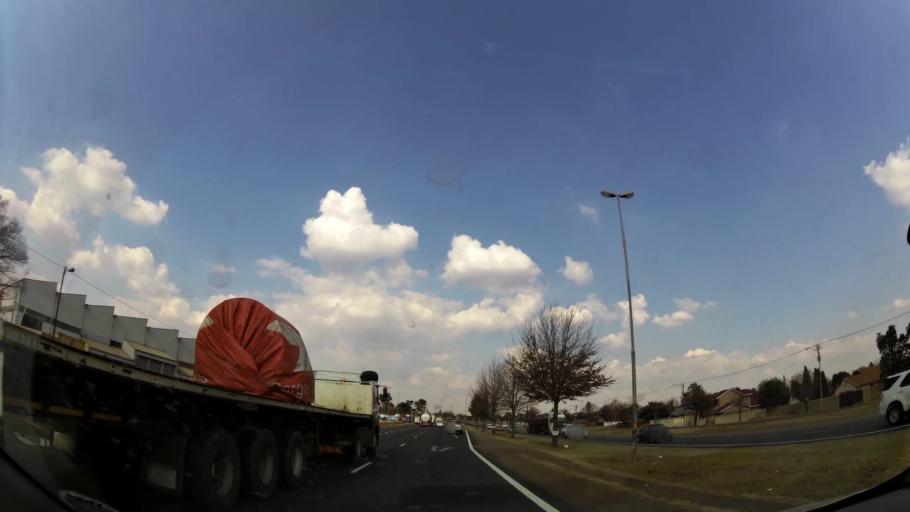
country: ZA
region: Gauteng
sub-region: Ekurhuleni Metropolitan Municipality
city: Germiston
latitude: -26.2963
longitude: 28.1763
